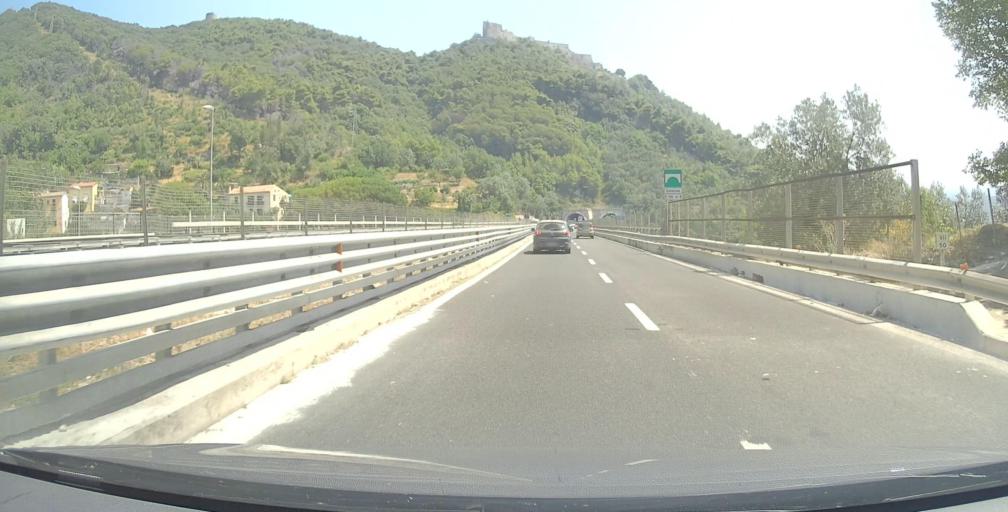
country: IT
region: Campania
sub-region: Provincia di Salerno
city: Vietri sul Mare
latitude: 40.6818
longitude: 14.7498
